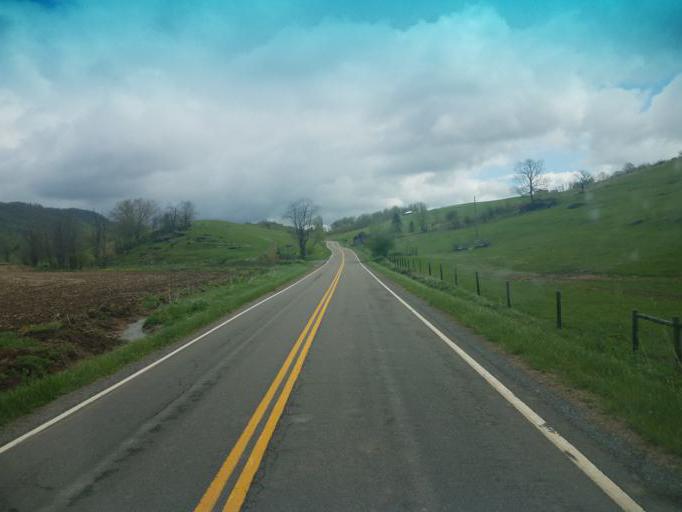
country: US
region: Virginia
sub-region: Smyth County
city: Atkins
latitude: 37.0006
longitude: -81.3752
